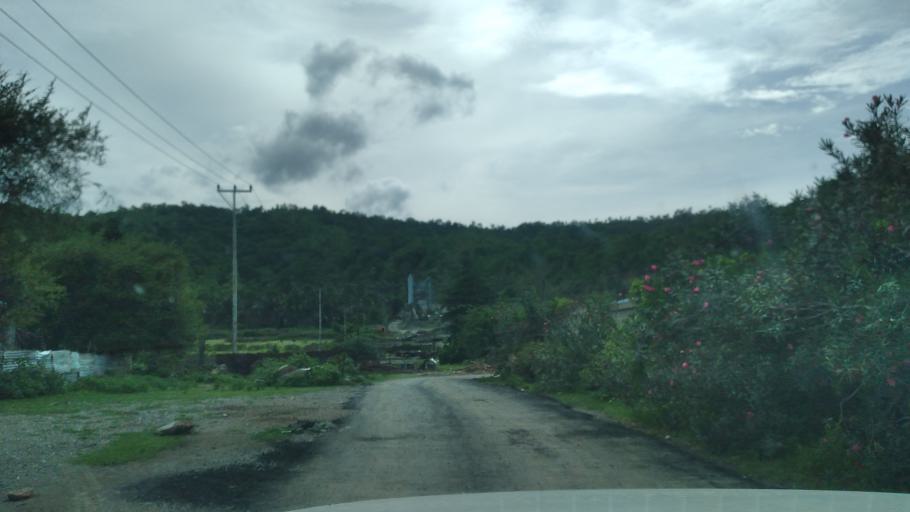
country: TL
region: Dili
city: Dili
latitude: -8.5983
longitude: 125.4804
